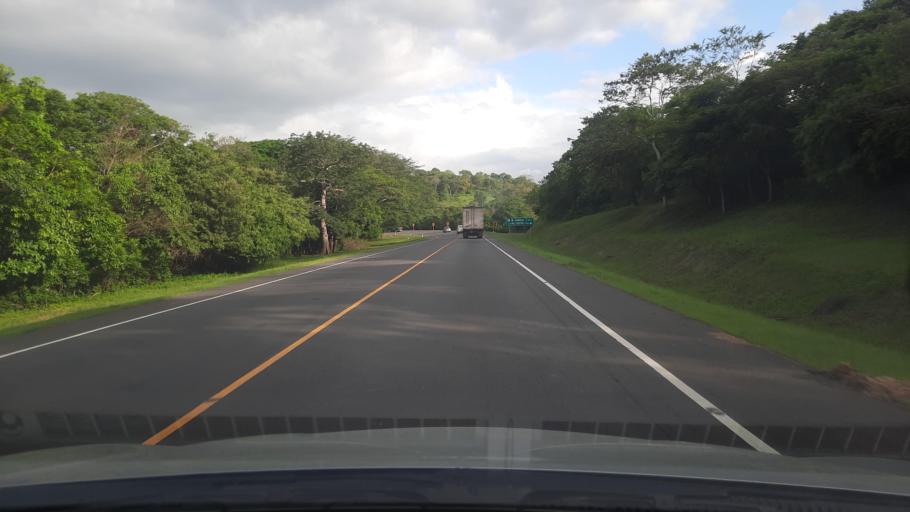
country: NI
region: Leon
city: La Paz Centro
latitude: 12.3631
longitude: -86.6651
